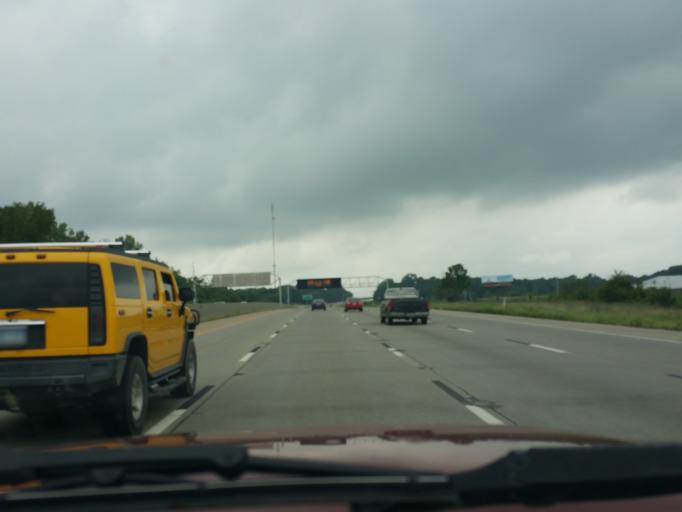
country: US
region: Kansas
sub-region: Johnson County
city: Merriam
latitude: 39.0695
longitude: -94.6802
